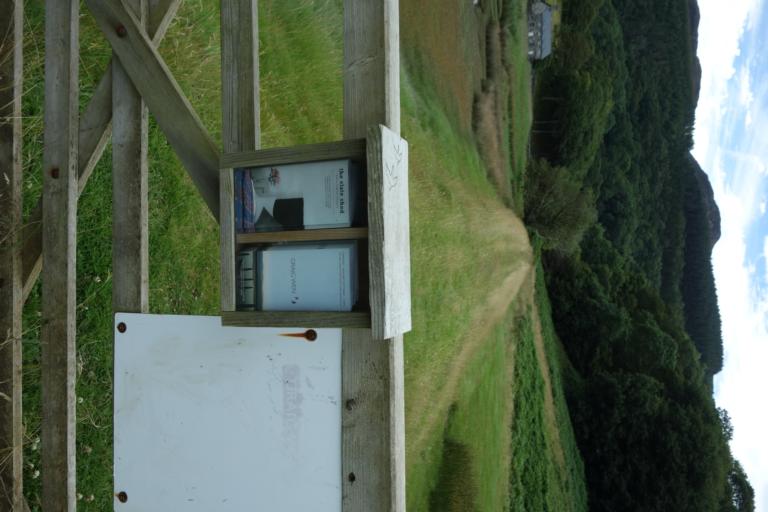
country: GB
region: Wales
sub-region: Gwynedd
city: Barmouth
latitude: 52.7250
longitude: -3.9976
